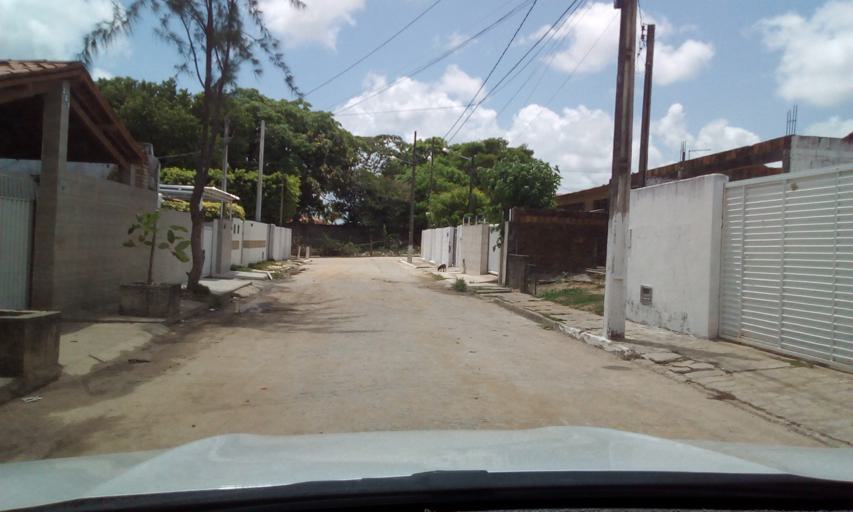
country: BR
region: Paraiba
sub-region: Joao Pessoa
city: Joao Pessoa
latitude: -7.1864
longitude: -34.8710
